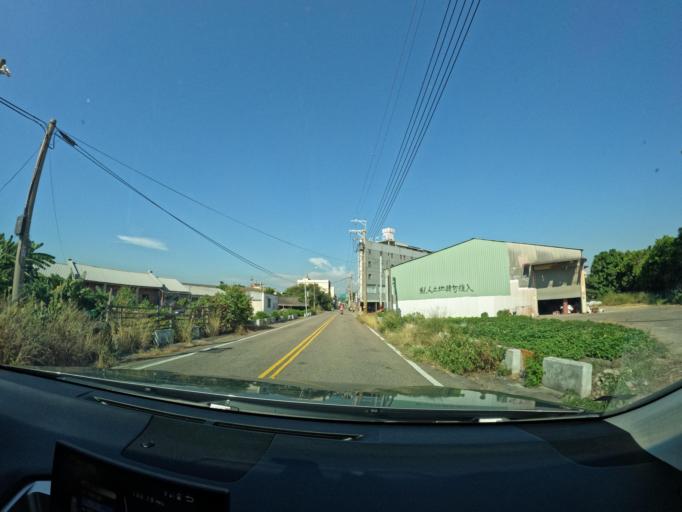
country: TW
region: Taiwan
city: Fengyuan
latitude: 24.2629
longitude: 120.5431
